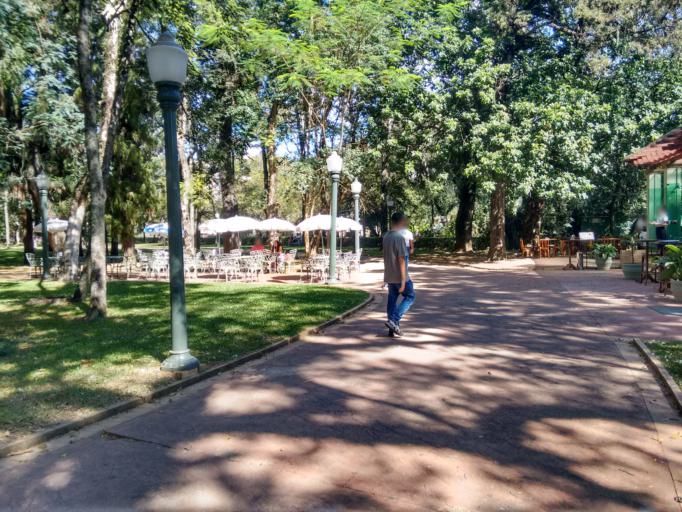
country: BR
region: Minas Gerais
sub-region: Pocos De Caldas
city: Pocos de Caldas
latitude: -21.7858
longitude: -46.5712
